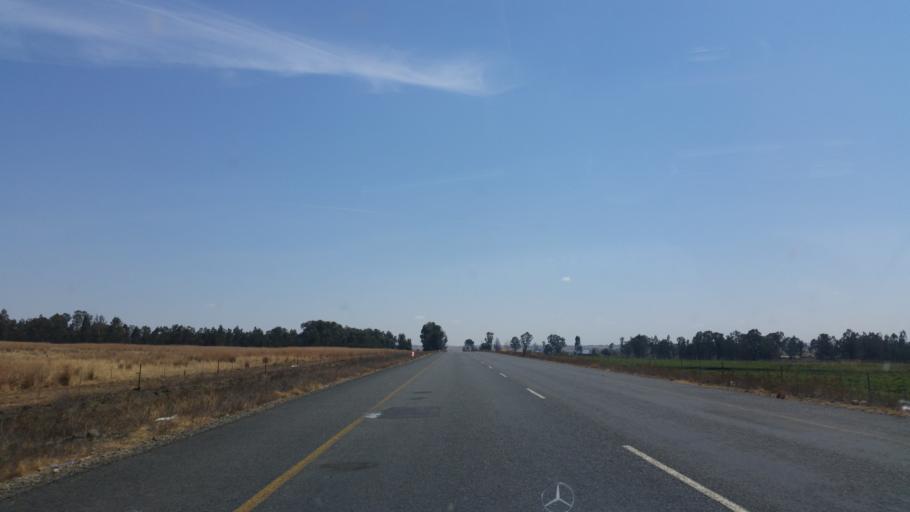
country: ZA
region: Orange Free State
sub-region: Thabo Mofutsanyana District Municipality
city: Phuthaditjhaba
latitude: -28.2162
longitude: 28.6966
